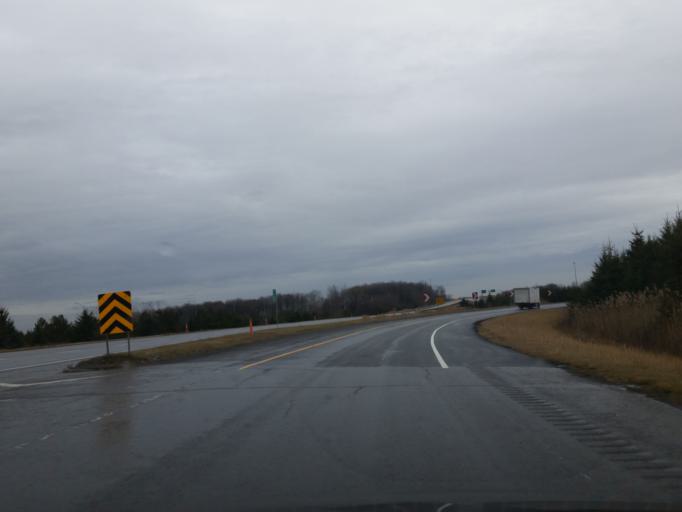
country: CA
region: Quebec
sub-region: Laurentides
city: Saint-Jerome
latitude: 45.7181
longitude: -73.9796
